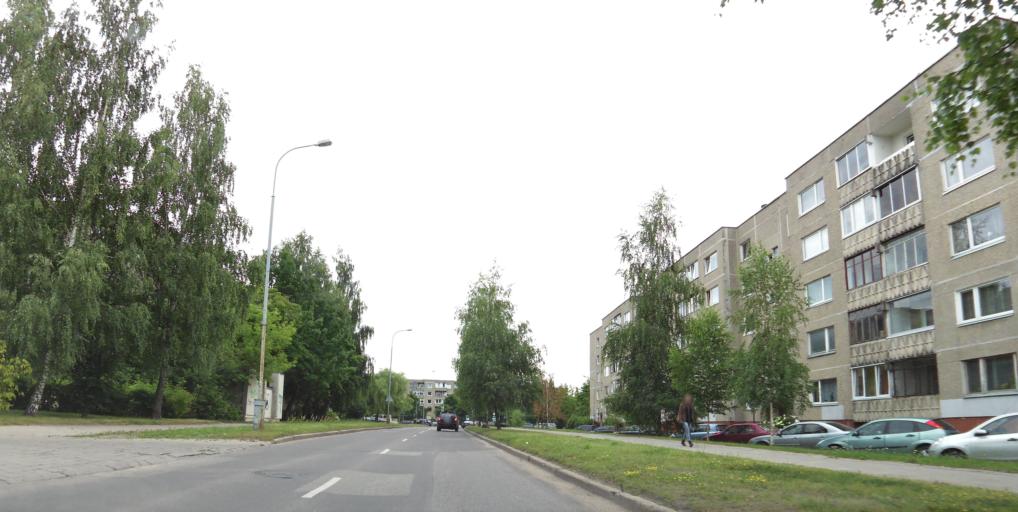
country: LT
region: Vilnius County
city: Seskine
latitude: 54.7163
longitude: 25.2555
